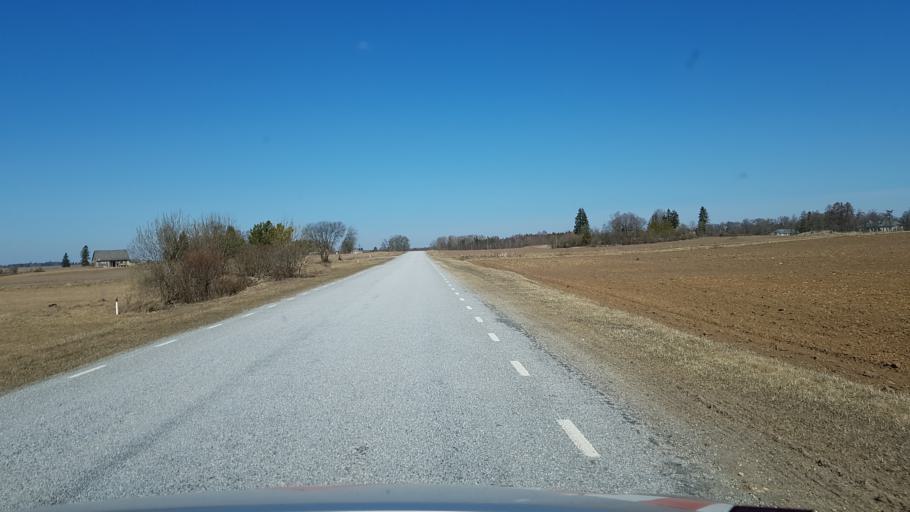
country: EE
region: Jaervamaa
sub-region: Koeru vald
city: Koeru
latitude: 59.0321
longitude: 26.0909
